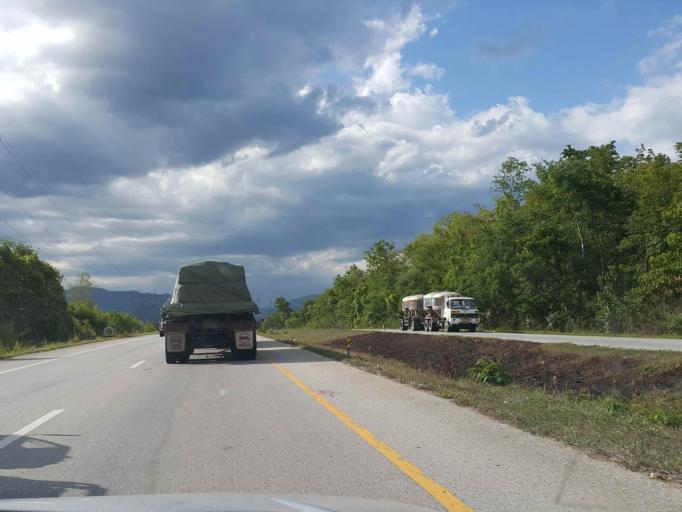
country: TH
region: Lampang
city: Thoen
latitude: 17.7047
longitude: 99.2310
